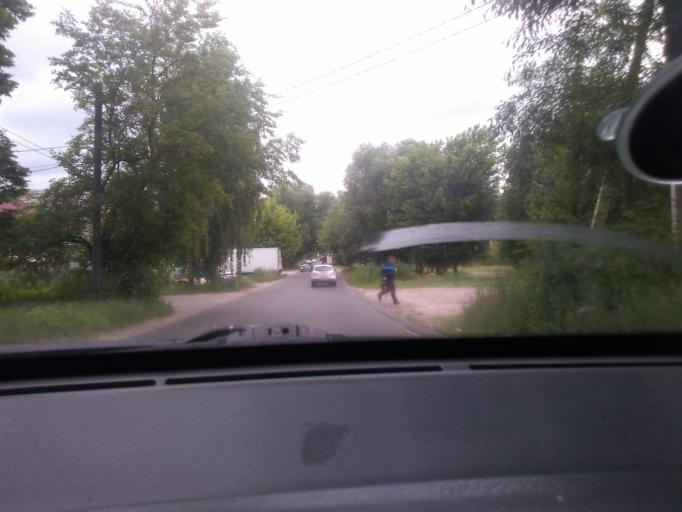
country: RU
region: Kursk
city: Kursk
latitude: 51.7380
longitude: 36.1763
